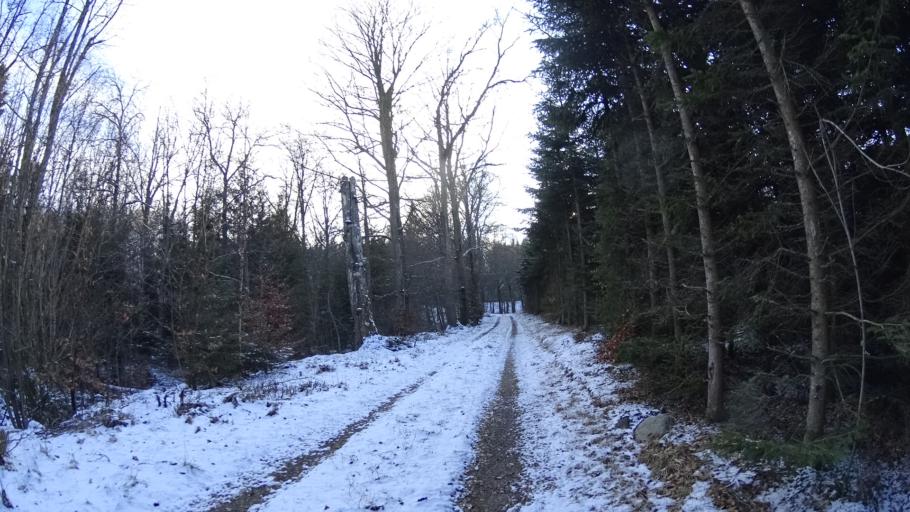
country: SE
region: Skane
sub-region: Hoors Kommun
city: Hoeoer
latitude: 55.9929
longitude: 13.5542
